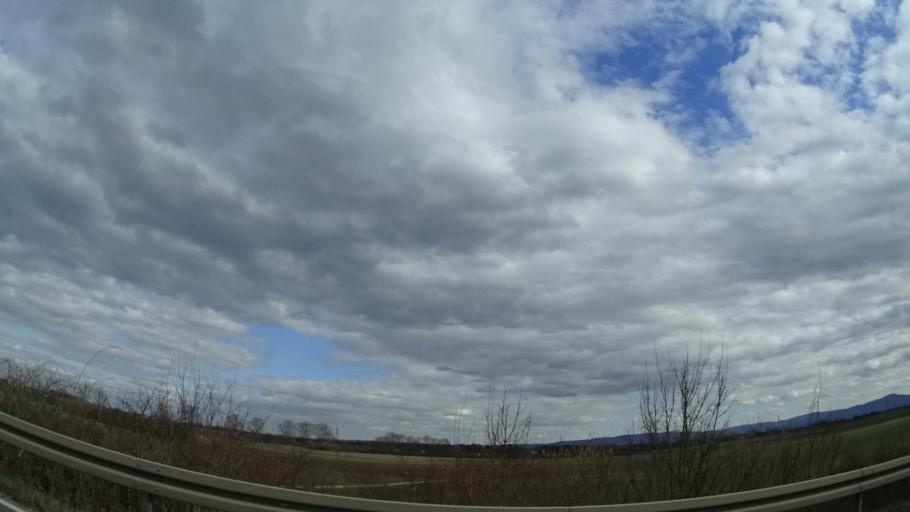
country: DE
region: Hesse
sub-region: Regierungsbezirk Darmstadt
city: Stockstadt am Rhein
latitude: 49.8187
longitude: 8.4807
